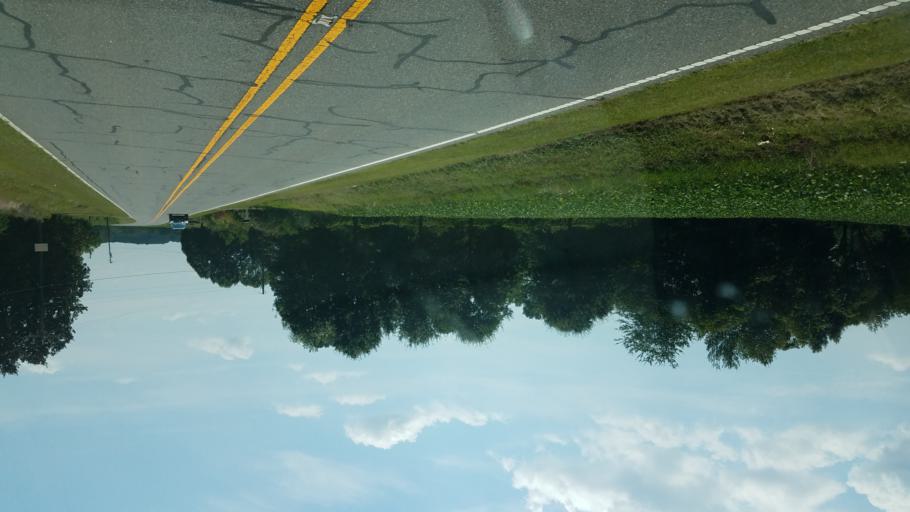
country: US
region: North Carolina
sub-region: Gaston County
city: Cherryville
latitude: 35.4294
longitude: -81.4139
